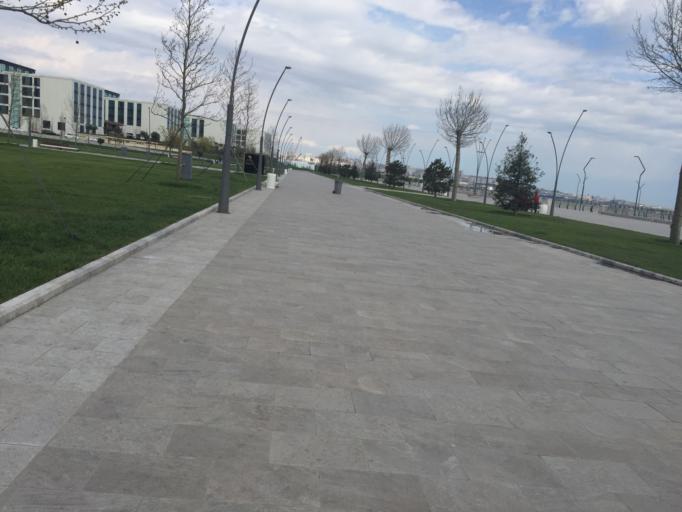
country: AZ
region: Baki
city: Baku
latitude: 40.3744
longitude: 49.8801
